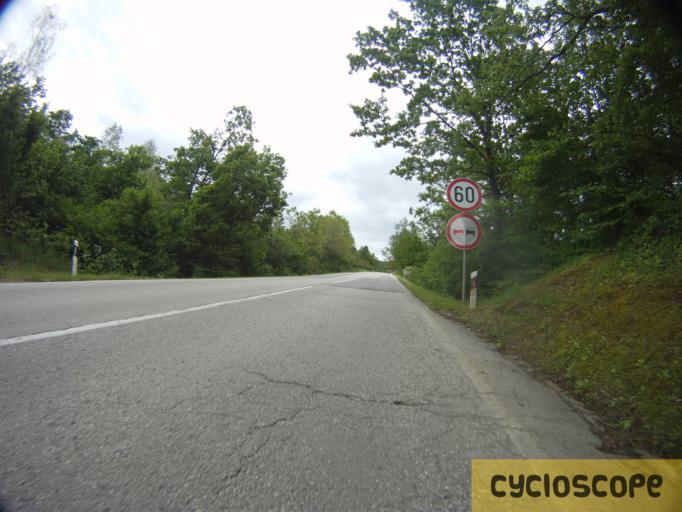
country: HR
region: Karlovacka
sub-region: Grad Karlovac
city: Karlovac
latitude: 45.4475
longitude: 15.3760
